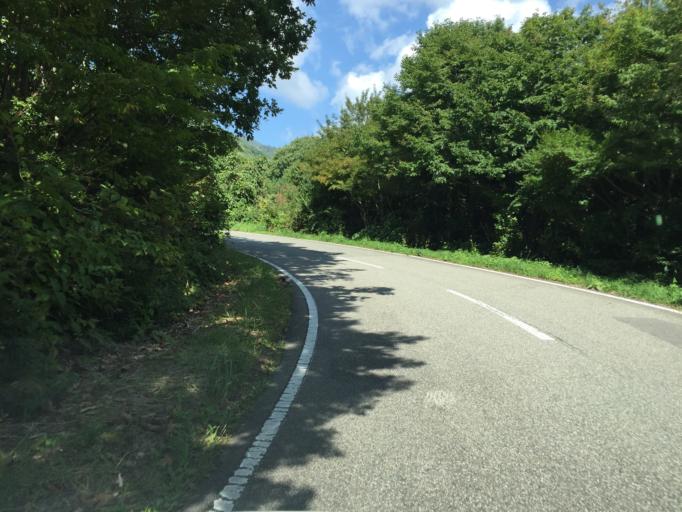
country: JP
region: Fukushima
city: Inawashiro
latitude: 37.5824
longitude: 140.0274
